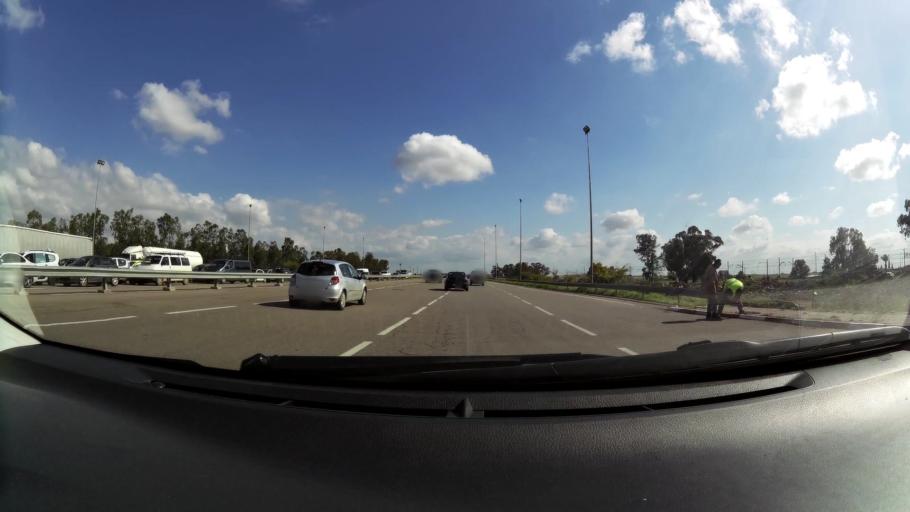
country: MA
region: Chaouia-Ouardigha
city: Nouaseur
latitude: 33.3657
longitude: -7.6201
